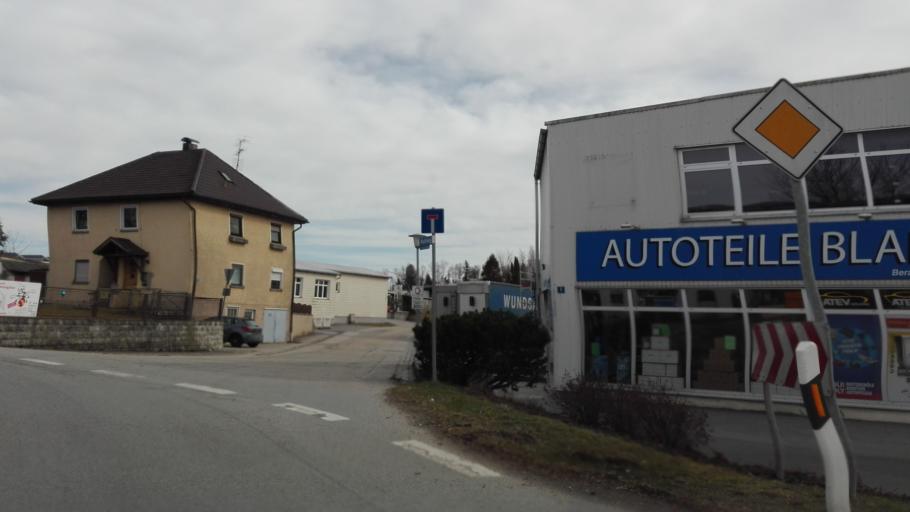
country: DE
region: Bavaria
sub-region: Lower Bavaria
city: Hauzenberg
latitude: 48.6300
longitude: 13.6420
